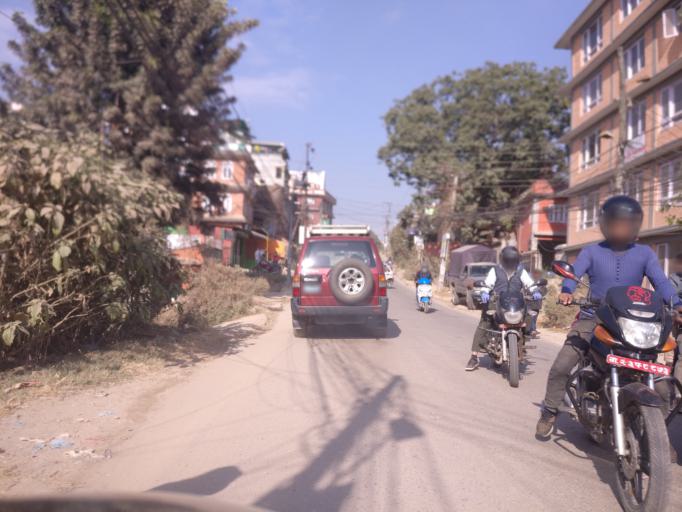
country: NP
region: Central Region
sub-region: Bagmati Zone
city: Patan
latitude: 27.6695
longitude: 85.3065
